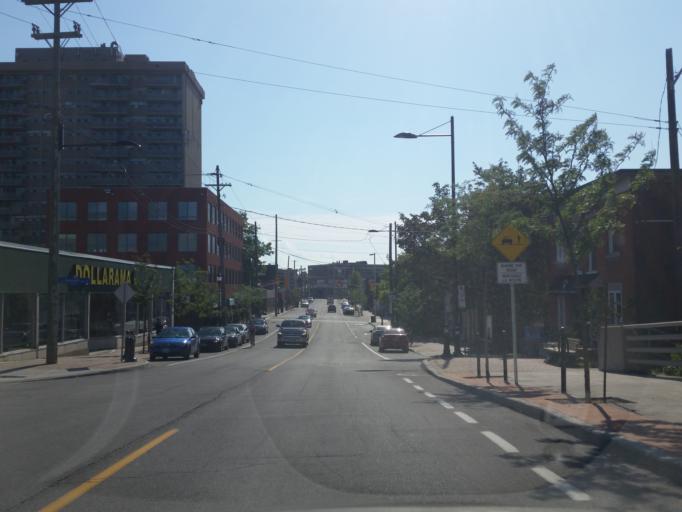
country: CA
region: Ontario
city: Ottawa
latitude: 45.4070
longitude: -75.7190
